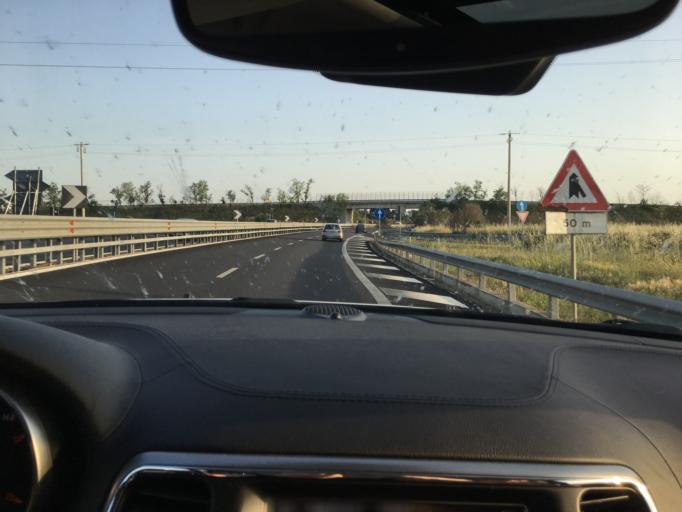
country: IT
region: Apulia
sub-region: Provincia di Lecce
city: Lequile
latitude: 40.2910
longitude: 18.1330
